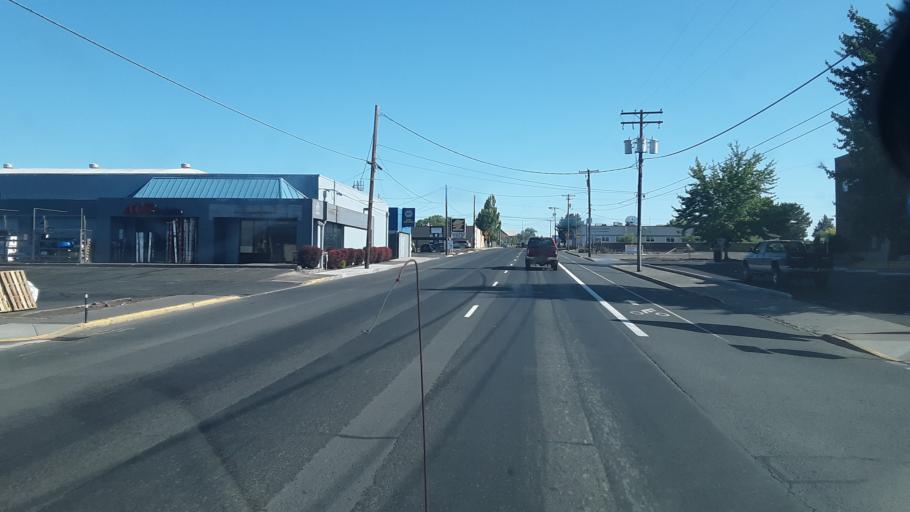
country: US
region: Oregon
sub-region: Jefferson County
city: Madras
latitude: 44.6277
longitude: -121.1306
